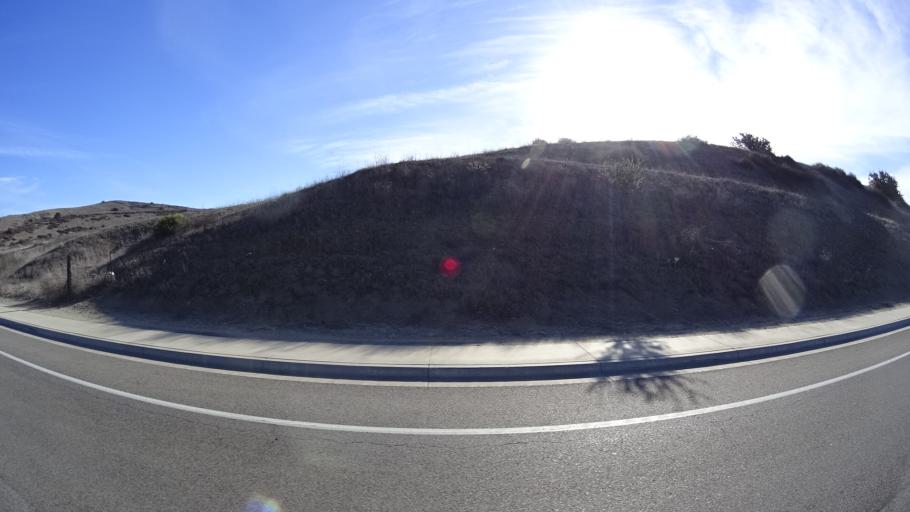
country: US
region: California
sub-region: Orange County
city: Las Flores
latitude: 33.6046
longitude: -117.6204
